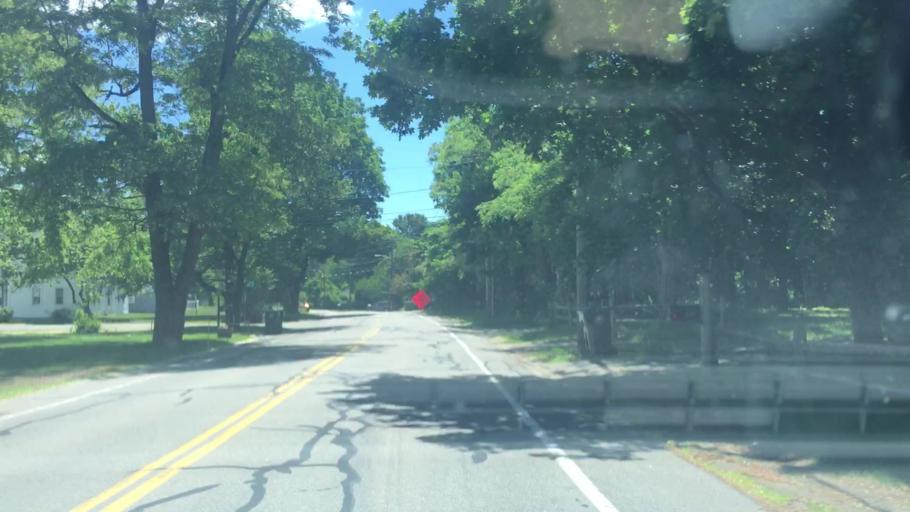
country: US
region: Maine
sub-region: York County
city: Kennebunk
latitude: 43.3692
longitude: -70.5255
